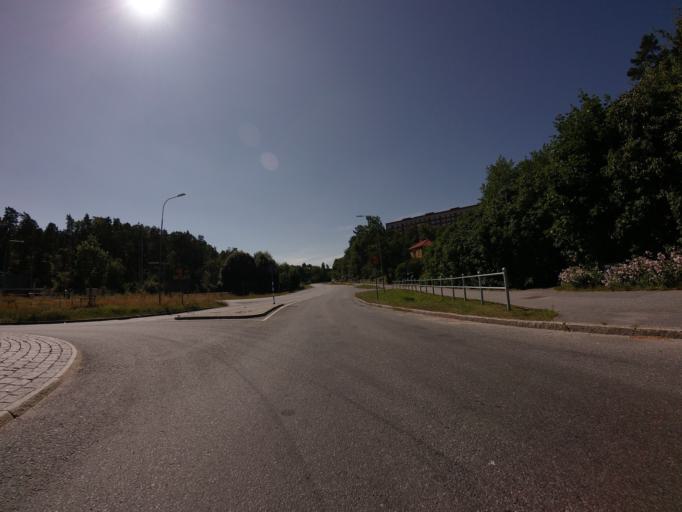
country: SE
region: Stockholm
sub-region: Lidingo
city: Brevik
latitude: 59.3563
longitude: 18.2227
